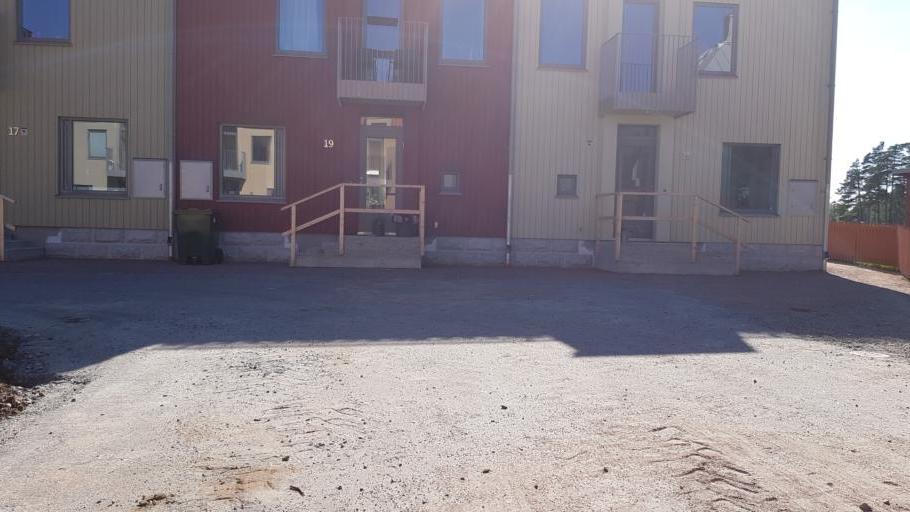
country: SE
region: Vaestra Goetaland
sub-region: Partille Kommun
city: Furulund
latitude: 57.6999
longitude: 12.1452
